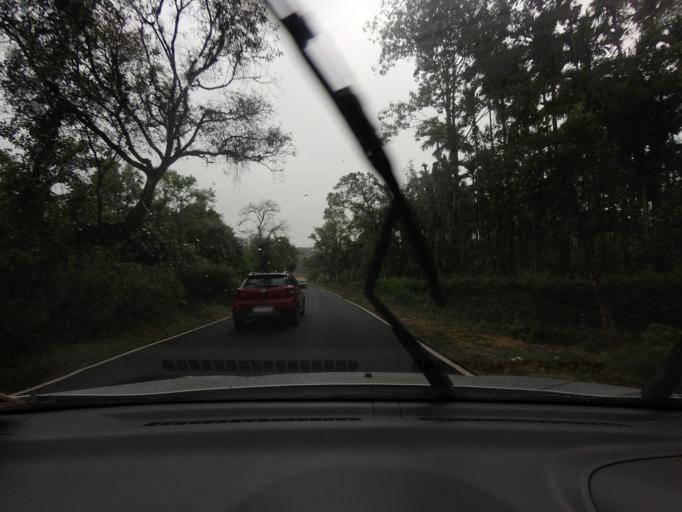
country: IN
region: Karnataka
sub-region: Hassan
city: Sakleshpur
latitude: 12.9782
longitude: 75.7204
